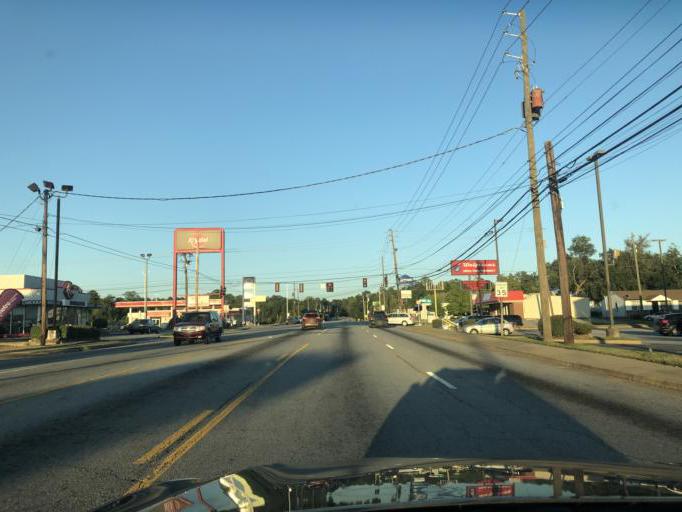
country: US
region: Georgia
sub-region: Muscogee County
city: Columbus
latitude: 32.4675
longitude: -84.9124
